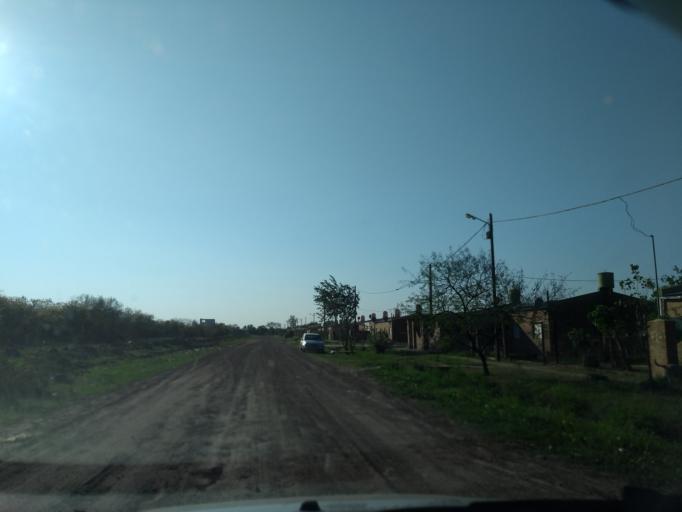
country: AR
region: Chaco
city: Fontana
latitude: -27.4166
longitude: -59.0541
